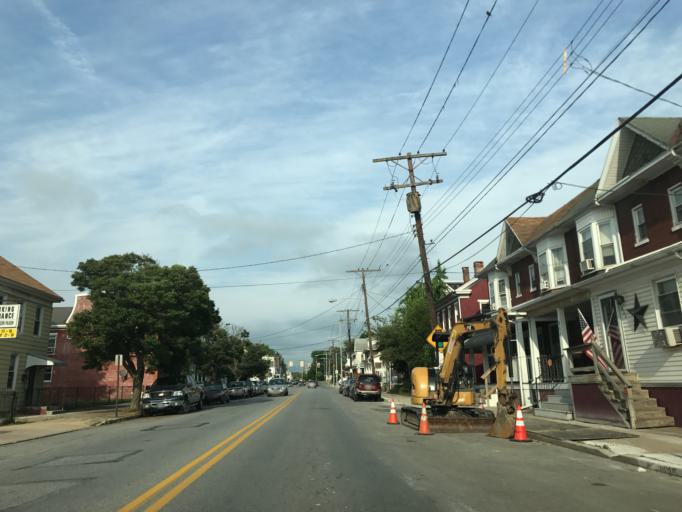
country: US
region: Pennsylvania
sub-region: York County
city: Valley View
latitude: 39.9612
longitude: -76.7104
